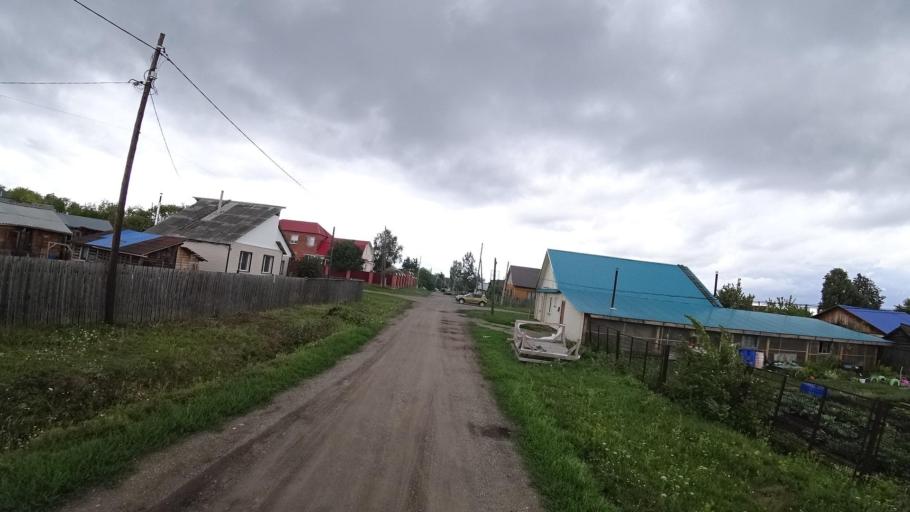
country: RU
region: Sverdlovsk
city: Kamyshlov
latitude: 56.8540
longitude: 62.6903
